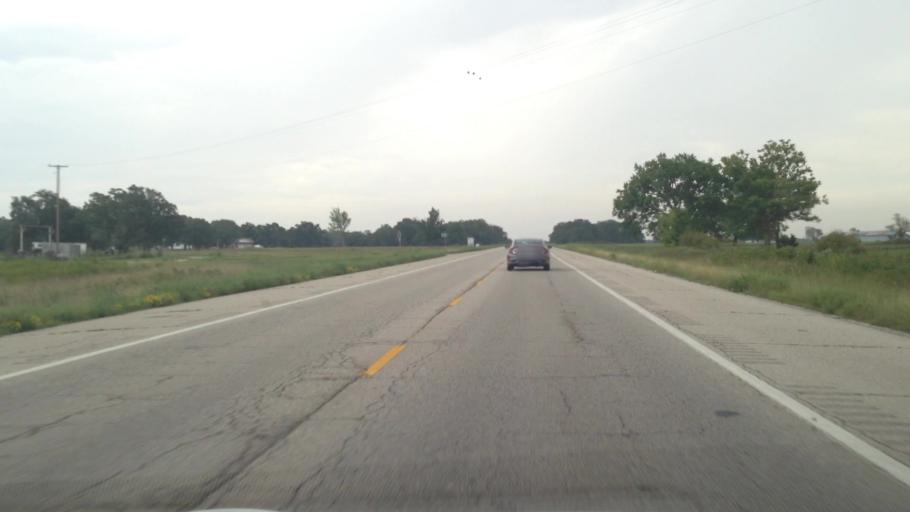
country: US
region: Kansas
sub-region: Cherokee County
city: Galena
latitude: 37.0176
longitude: -94.6364
